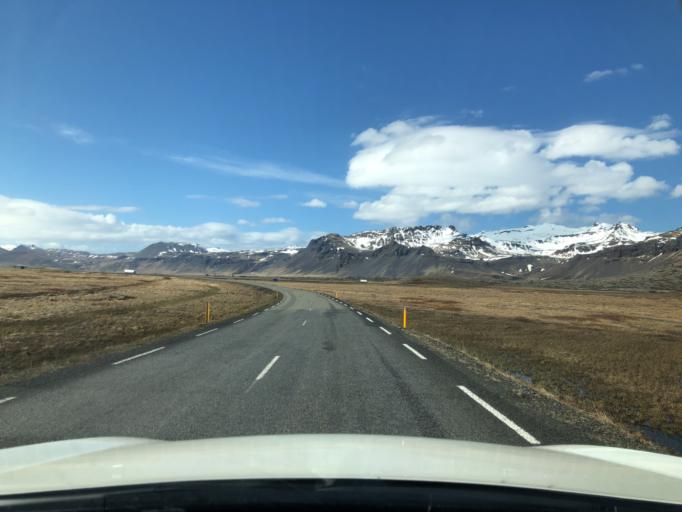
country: IS
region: West
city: Olafsvik
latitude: 64.8275
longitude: -23.2277
